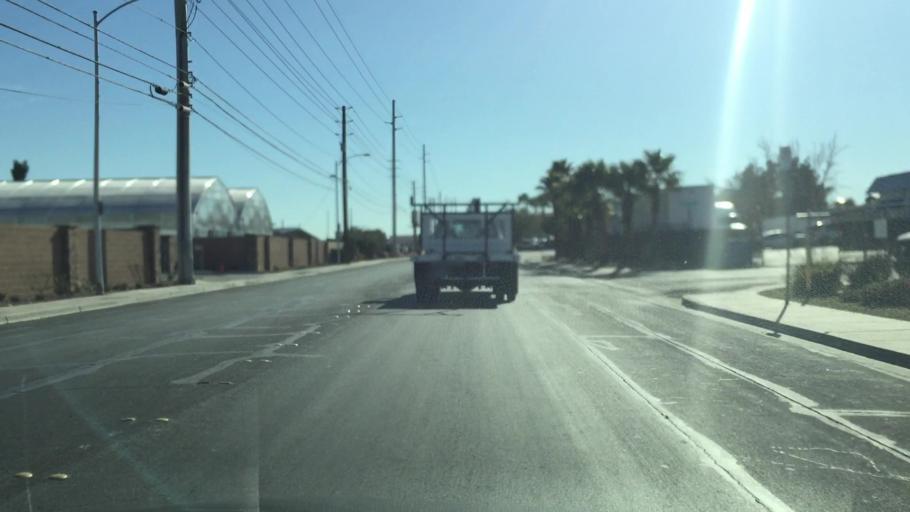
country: US
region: Nevada
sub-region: Clark County
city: Paradise
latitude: 36.1035
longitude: -115.1946
